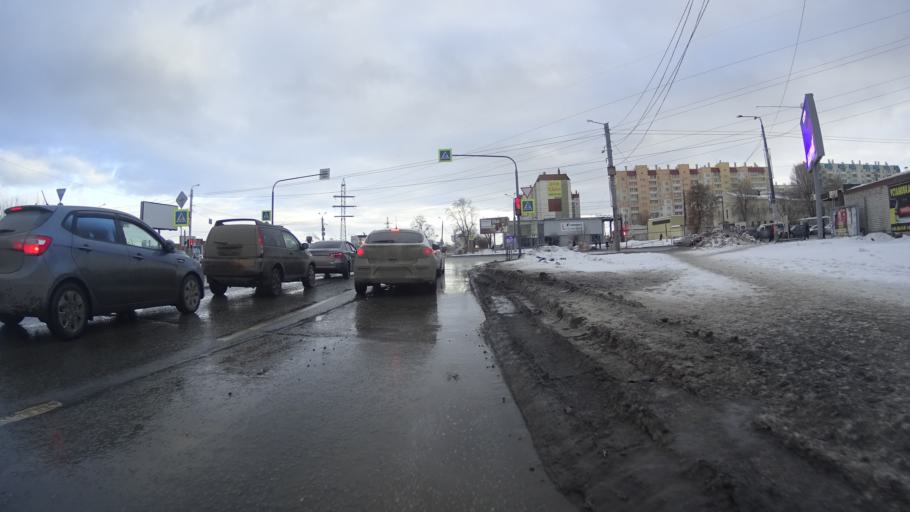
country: RU
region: Chelyabinsk
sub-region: Gorod Chelyabinsk
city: Chelyabinsk
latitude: 55.1386
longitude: 61.4019
